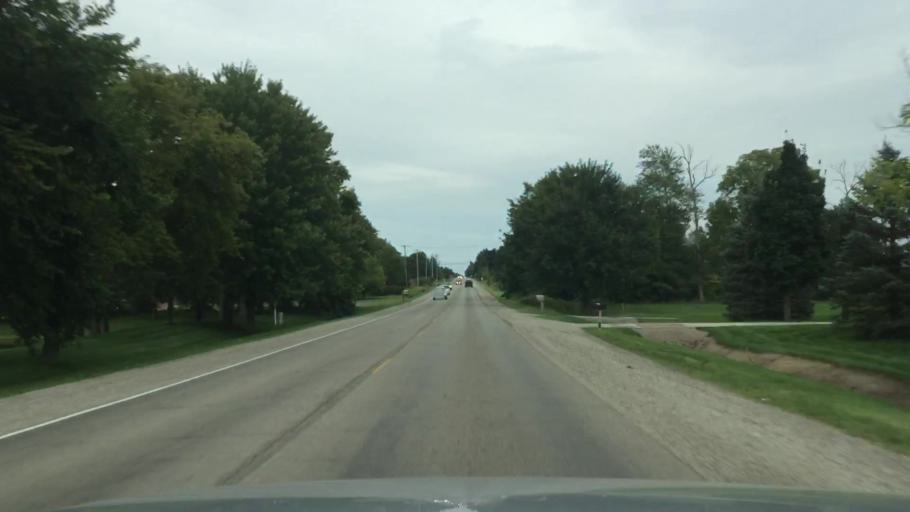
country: US
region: Michigan
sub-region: Genesee County
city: Grand Blanc
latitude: 42.8861
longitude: -83.6666
